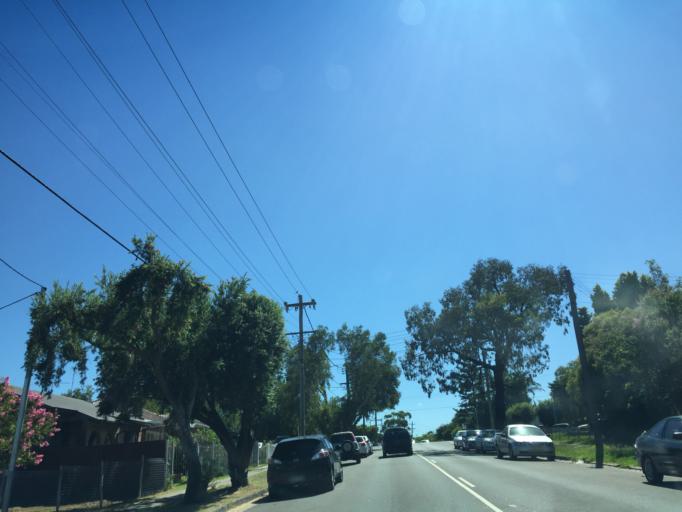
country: AU
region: New South Wales
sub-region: Blacktown
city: Blacktown
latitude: -33.7693
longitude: 150.9000
